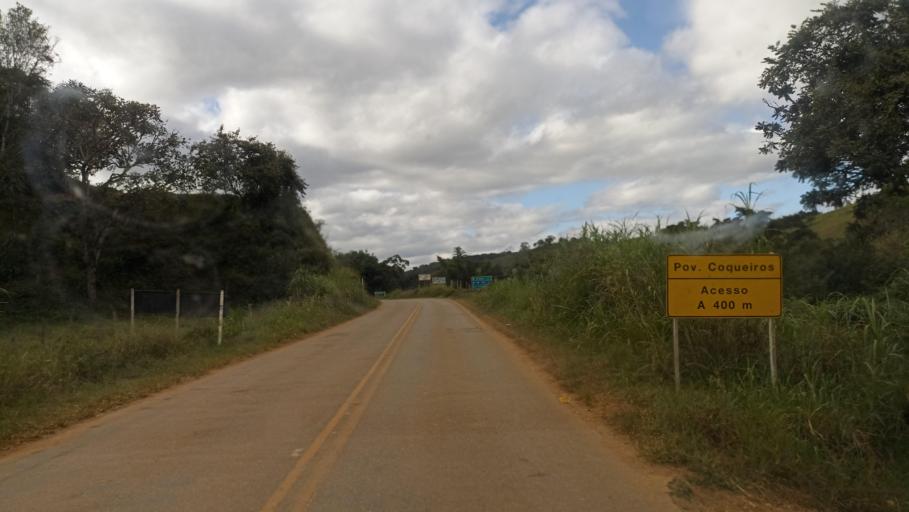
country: BR
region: Minas Gerais
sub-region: Tiradentes
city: Tiradentes
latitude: -21.0929
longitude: -44.0738
